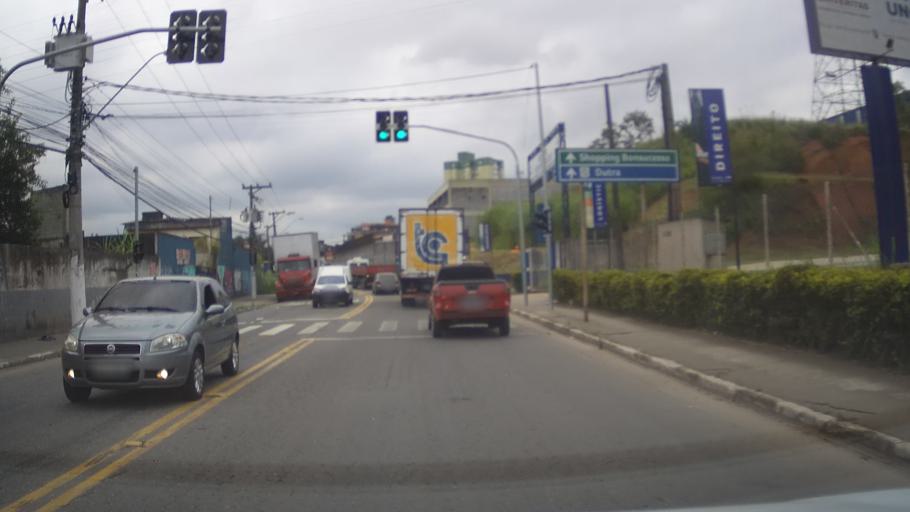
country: BR
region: Sao Paulo
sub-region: Itaquaquecetuba
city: Itaquaquecetuba
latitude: -23.4330
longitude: -46.4019
